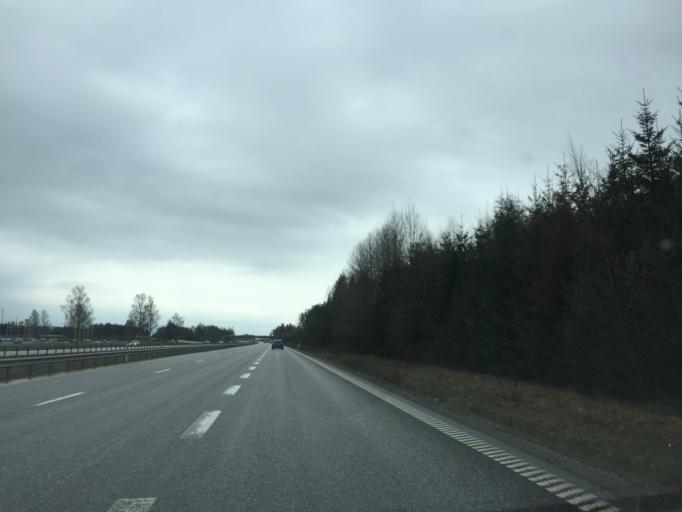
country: SE
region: OErebro
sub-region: Orebro Kommun
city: Orebro
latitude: 59.2199
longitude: 15.1351
